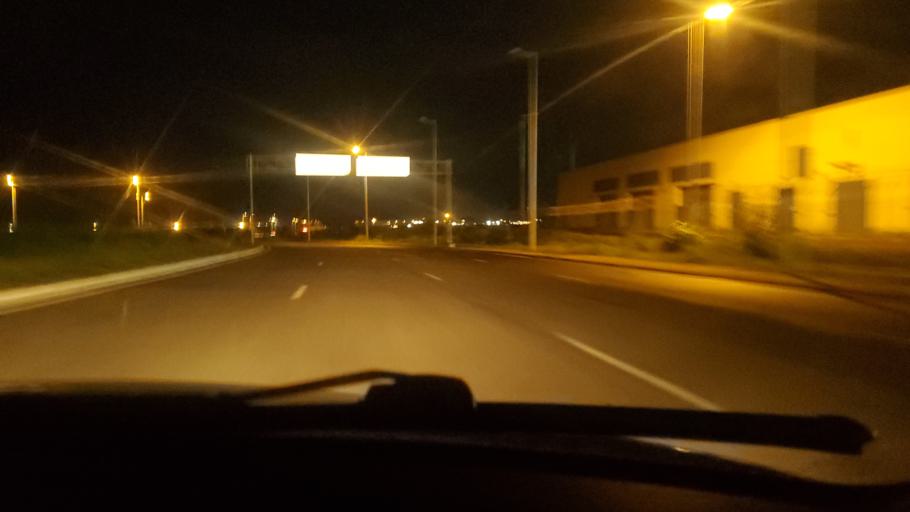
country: SN
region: Thies
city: Pout
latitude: 14.6663
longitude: -17.0658
